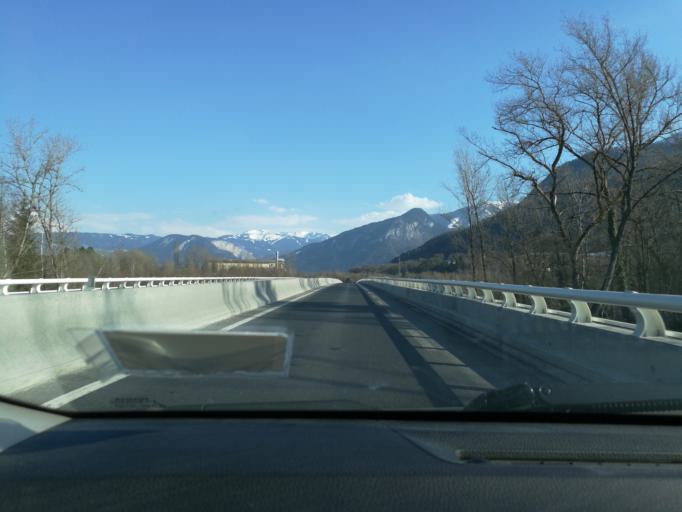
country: FR
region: Rhone-Alpes
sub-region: Departement de la Haute-Savoie
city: Vougy
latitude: 46.0727
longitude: 6.4882
